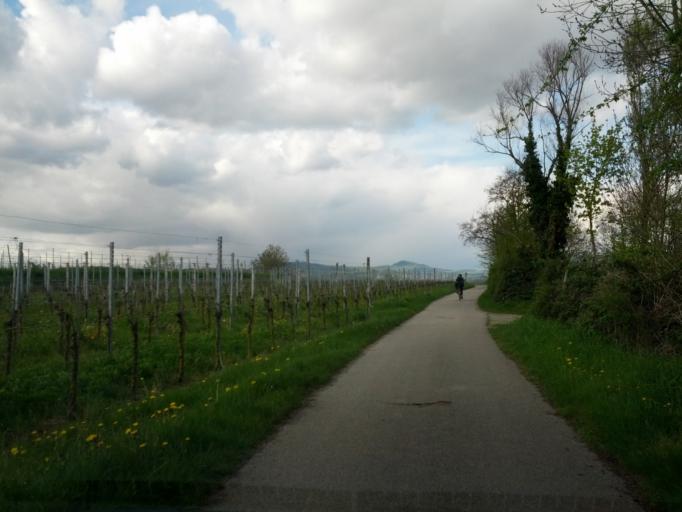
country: DE
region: Baden-Wuerttemberg
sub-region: Freiburg Region
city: Merdingen
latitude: 47.9900
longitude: 7.6776
